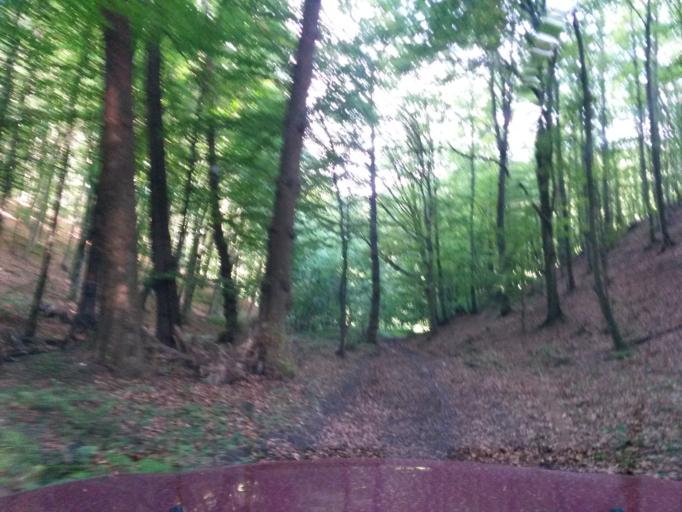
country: SK
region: Kosicky
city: Moldava nad Bodvou
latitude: 48.7277
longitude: 21.0758
